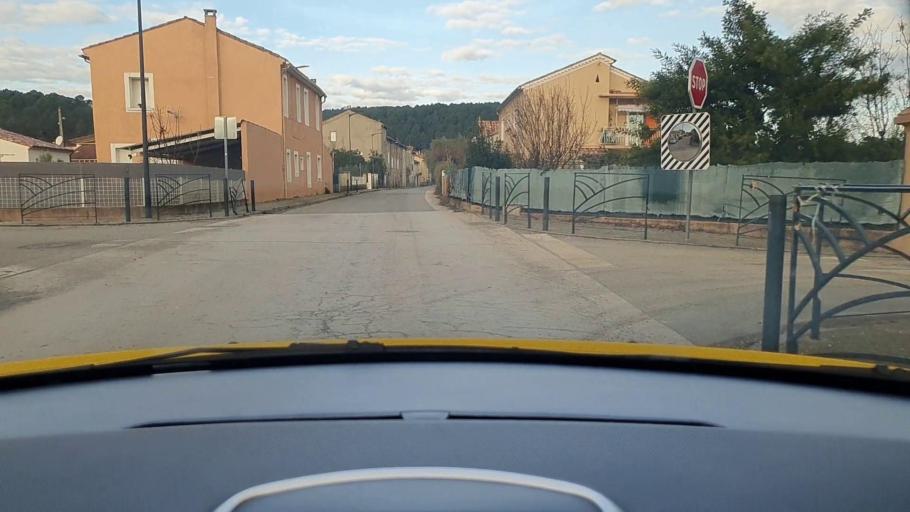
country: FR
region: Languedoc-Roussillon
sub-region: Departement du Gard
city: Laval-Pradel
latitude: 44.2302
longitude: 4.0602
